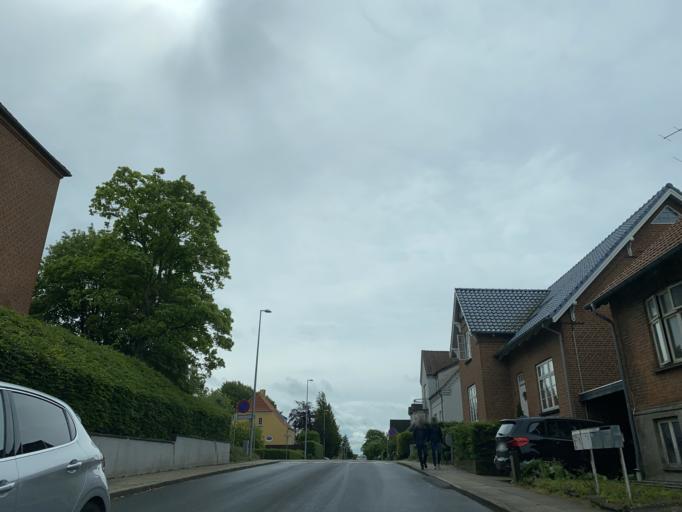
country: DK
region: Central Jutland
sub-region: Favrskov Kommune
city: Hammel
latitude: 56.2553
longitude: 9.8695
